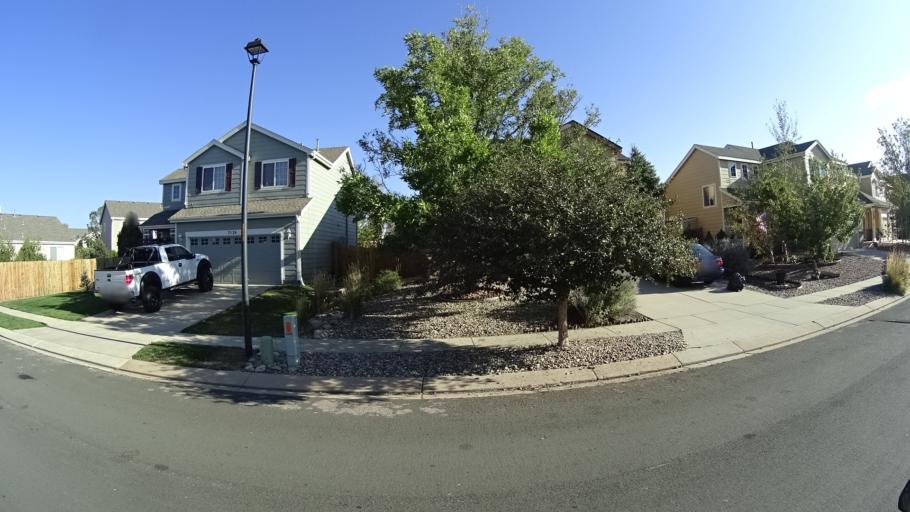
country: US
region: Colorado
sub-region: El Paso County
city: Cimarron Hills
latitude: 38.8828
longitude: -104.6942
